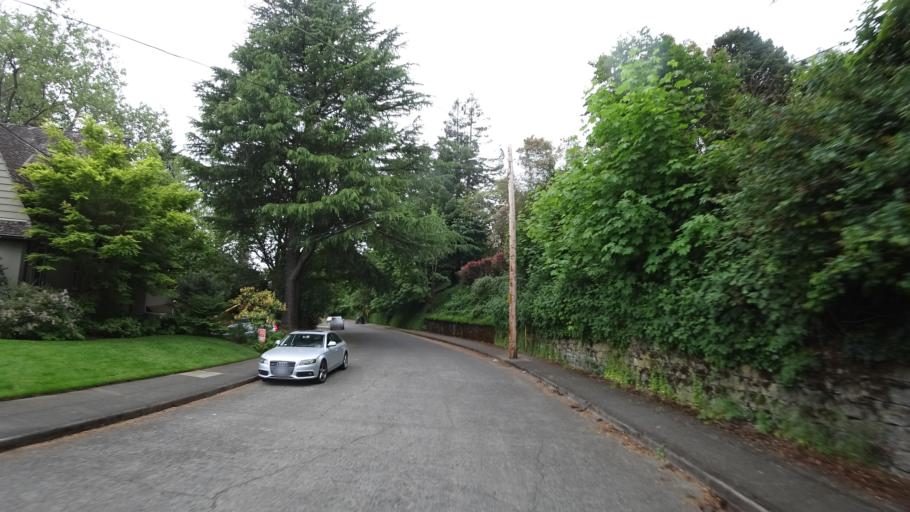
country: US
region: Oregon
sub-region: Multnomah County
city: Portland
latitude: 45.5462
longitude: -122.6270
